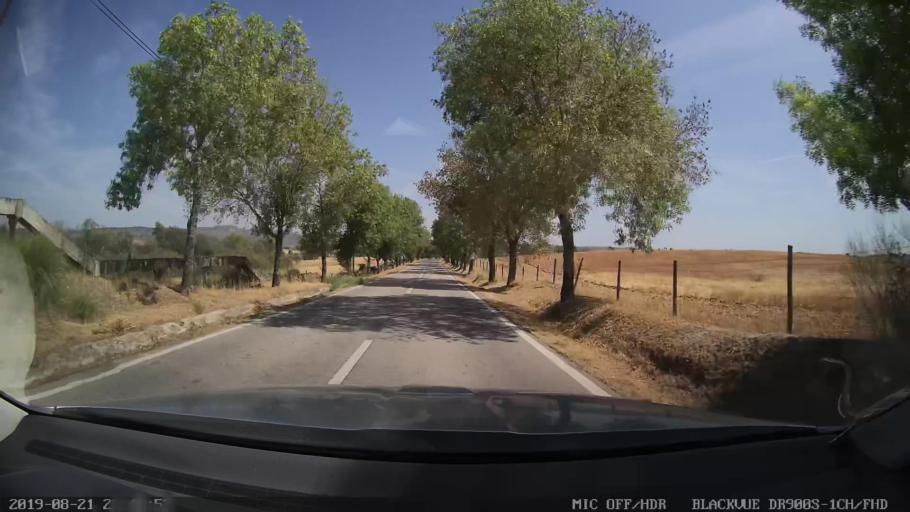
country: PT
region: Castelo Branco
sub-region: Idanha-A-Nova
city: Idanha-a-Nova
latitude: 39.8711
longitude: -7.2529
